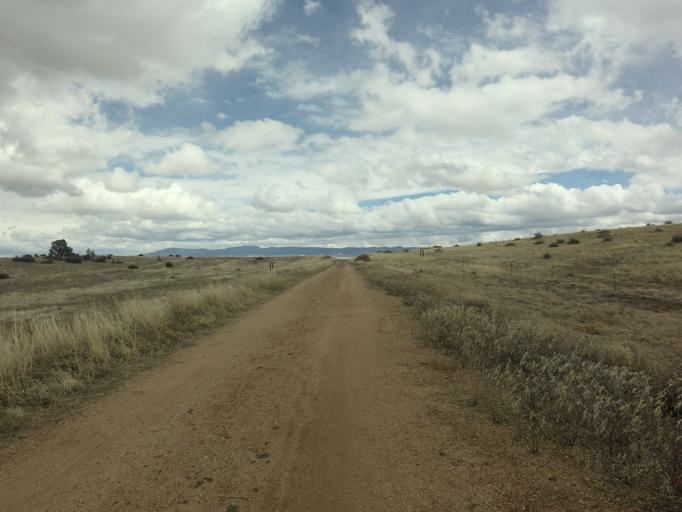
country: US
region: Arizona
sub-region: Yavapai County
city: Prescott Valley
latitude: 34.6113
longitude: -112.3800
